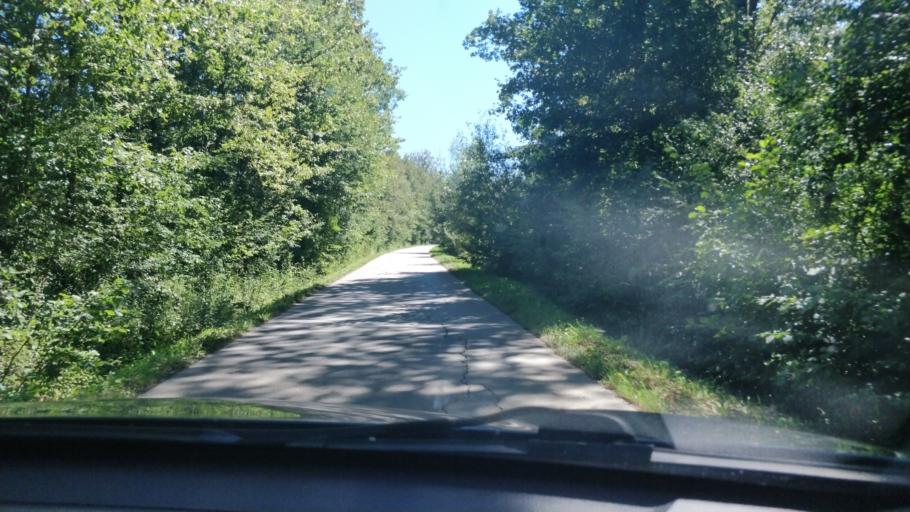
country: HR
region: Karlovacka
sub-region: Grad Karlovac
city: Karlovac
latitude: 45.4709
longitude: 15.6625
